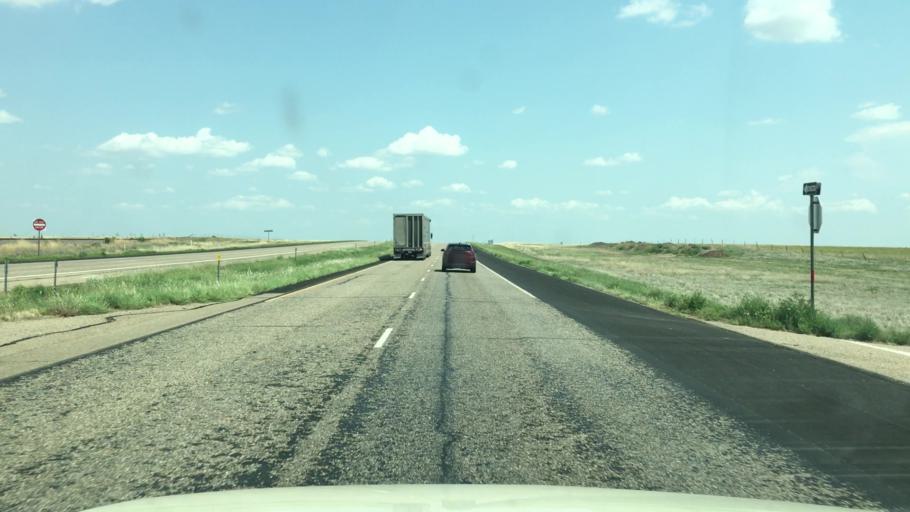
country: US
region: Texas
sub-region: Armstrong County
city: Claude
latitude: 35.1313
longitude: -101.4170
